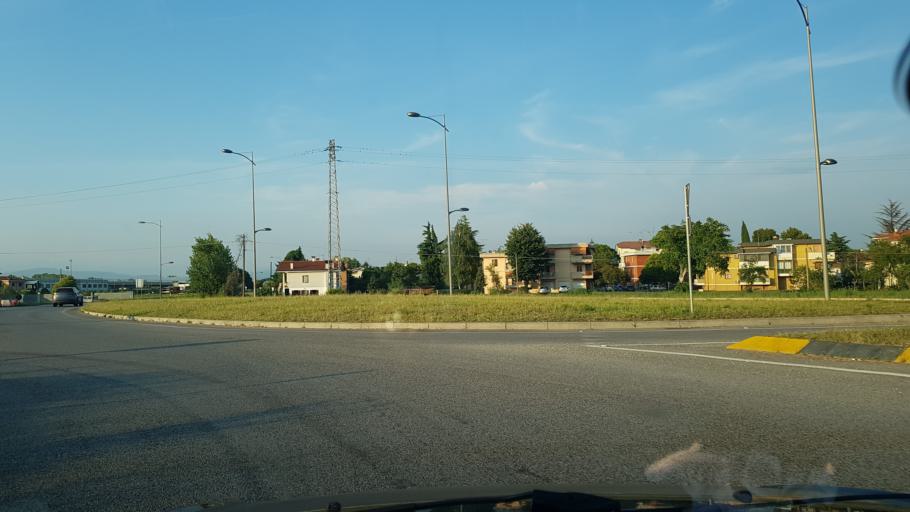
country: IT
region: Friuli Venezia Giulia
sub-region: Provincia di Gorizia
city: Villesse
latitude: 45.8649
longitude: 13.4402
